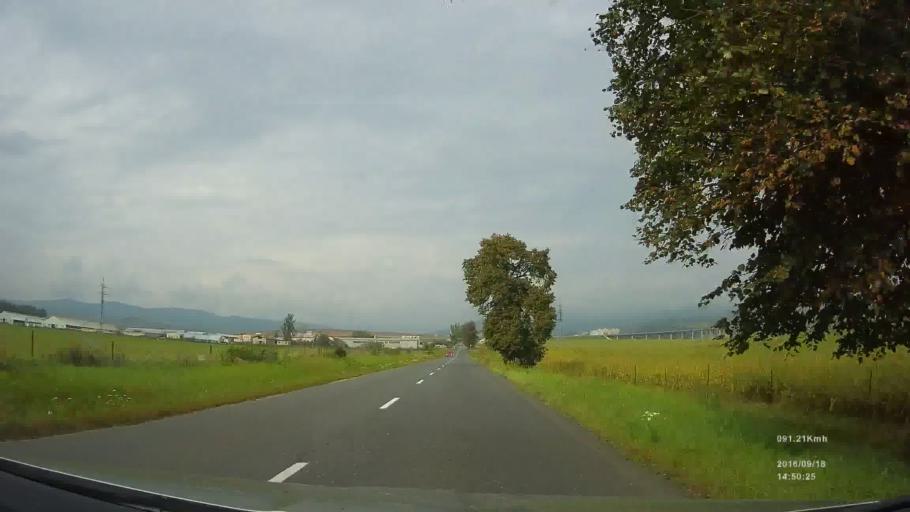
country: SK
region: Presovsky
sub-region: Okres Presov
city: Levoca
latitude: 48.9965
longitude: 20.5824
